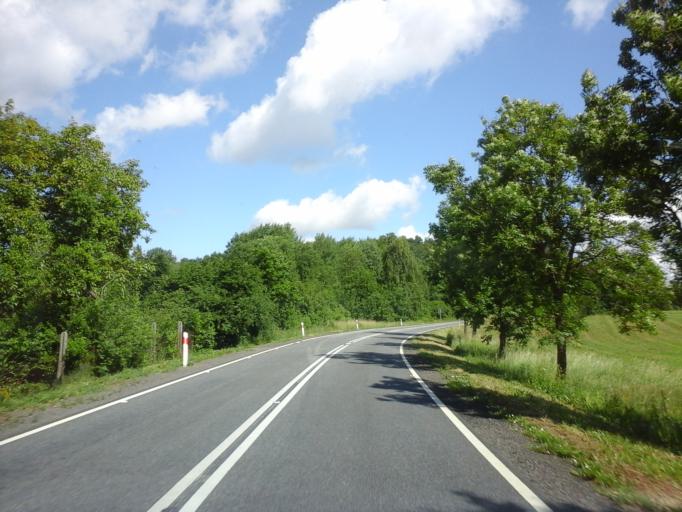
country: PL
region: West Pomeranian Voivodeship
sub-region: Powiat stargardzki
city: Insko
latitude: 53.4710
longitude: 15.5780
